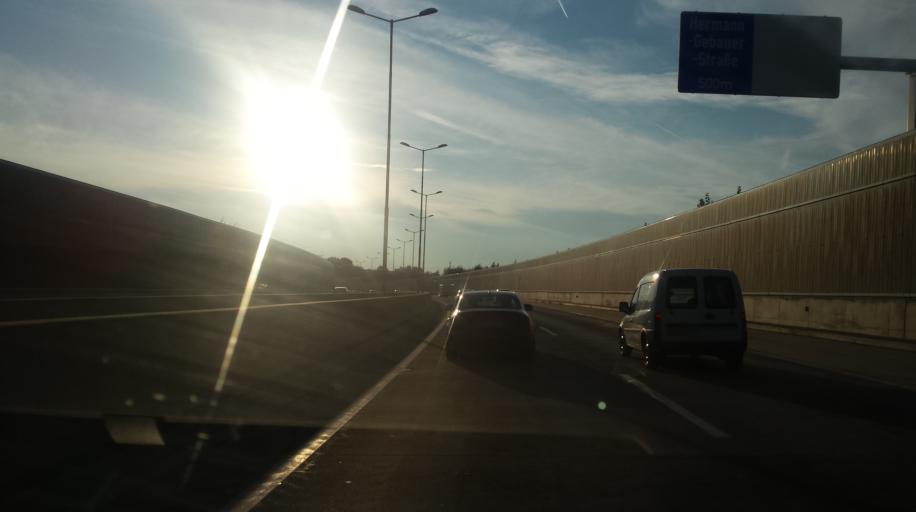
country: AT
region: Lower Austria
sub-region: Politischer Bezirk Wien-Umgebung
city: Gerasdorf bei Wien
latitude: 48.2679
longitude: 16.4892
